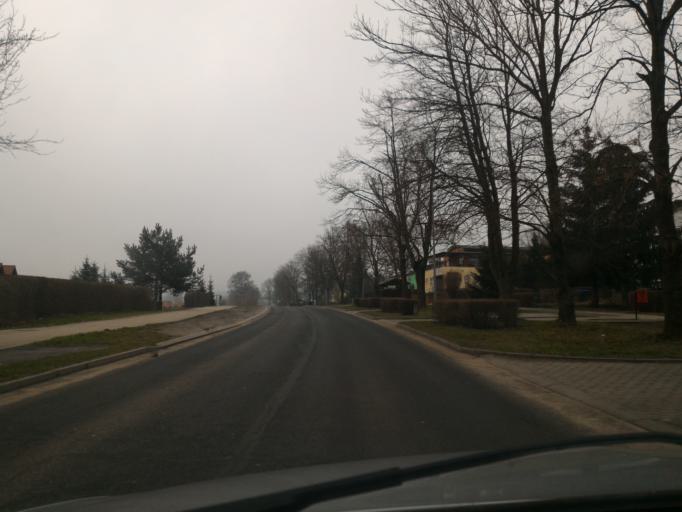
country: PL
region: Lower Silesian Voivodeship
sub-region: Powiat zgorzelecki
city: Bogatynia
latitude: 50.9077
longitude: 14.9597
